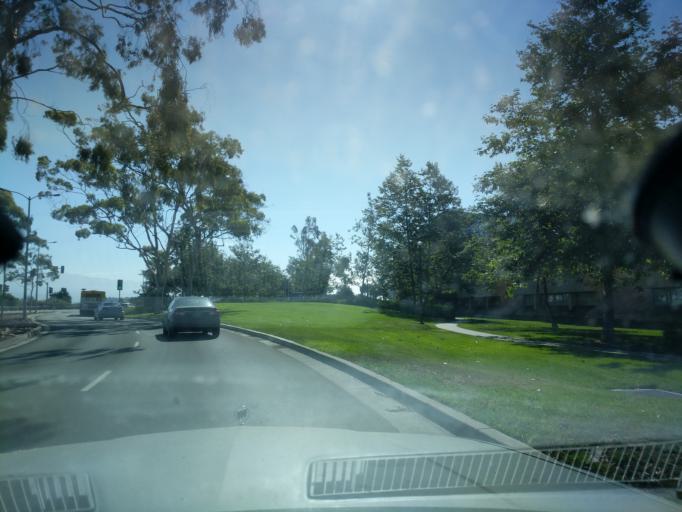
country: US
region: California
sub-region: Santa Barbara County
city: Isla Vista
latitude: 34.4160
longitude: -119.8417
